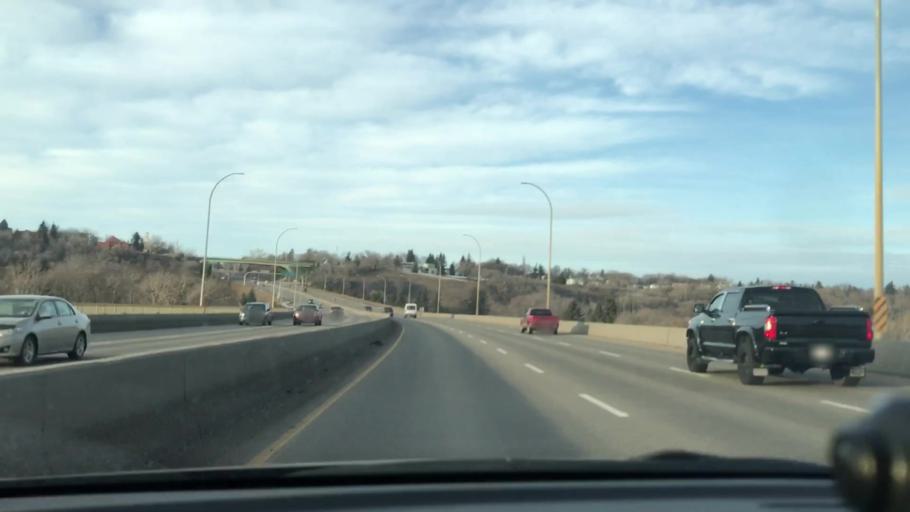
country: CA
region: Alberta
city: Edmonton
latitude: 53.5554
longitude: -113.4384
